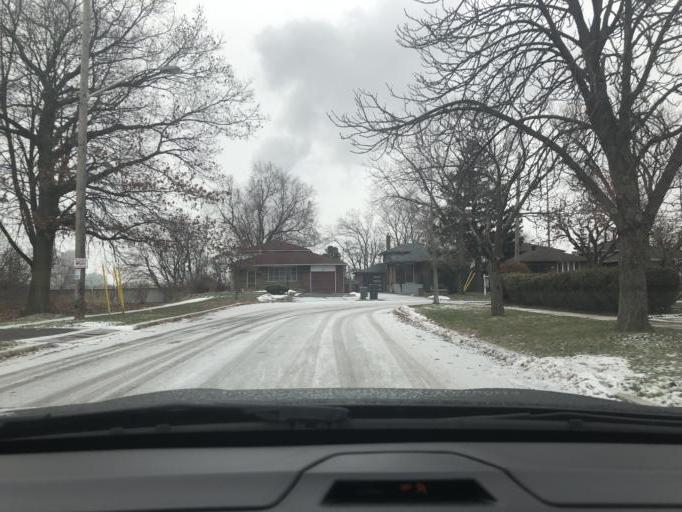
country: CA
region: Ontario
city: Scarborough
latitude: 43.7796
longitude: -79.2704
